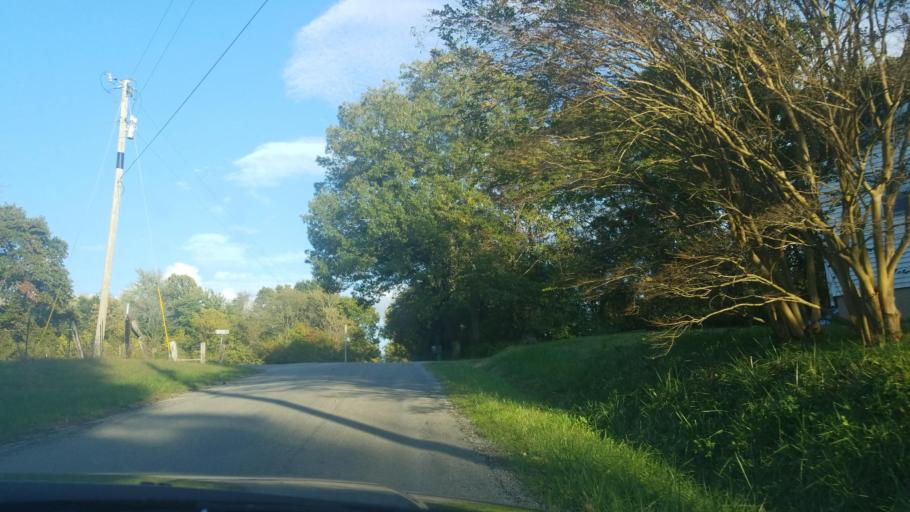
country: US
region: Illinois
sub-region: Williamson County
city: Marion
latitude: 37.7609
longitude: -88.8064
